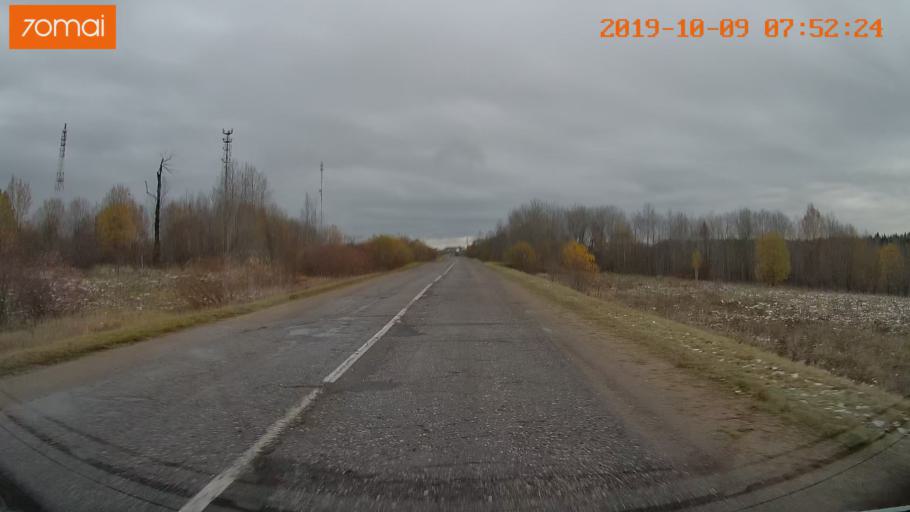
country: RU
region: Jaroslavl
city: Kukoboy
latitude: 58.6908
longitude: 39.8868
